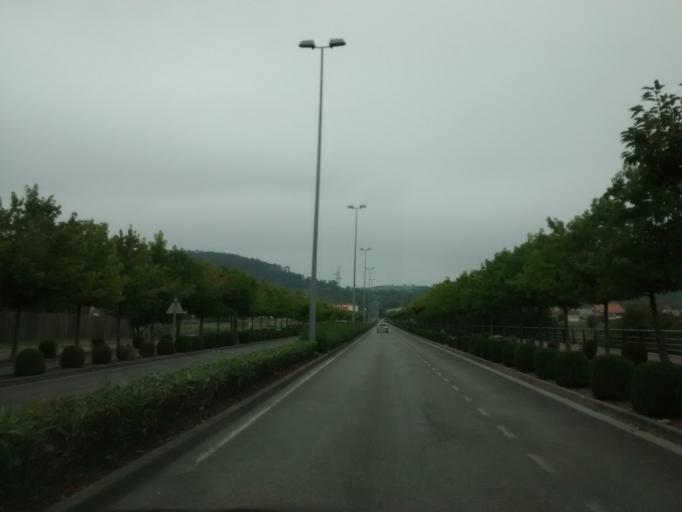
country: ES
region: Cantabria
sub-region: Provincia de Cantabria
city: Torrelavega
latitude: 43.3379
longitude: -4.0537
